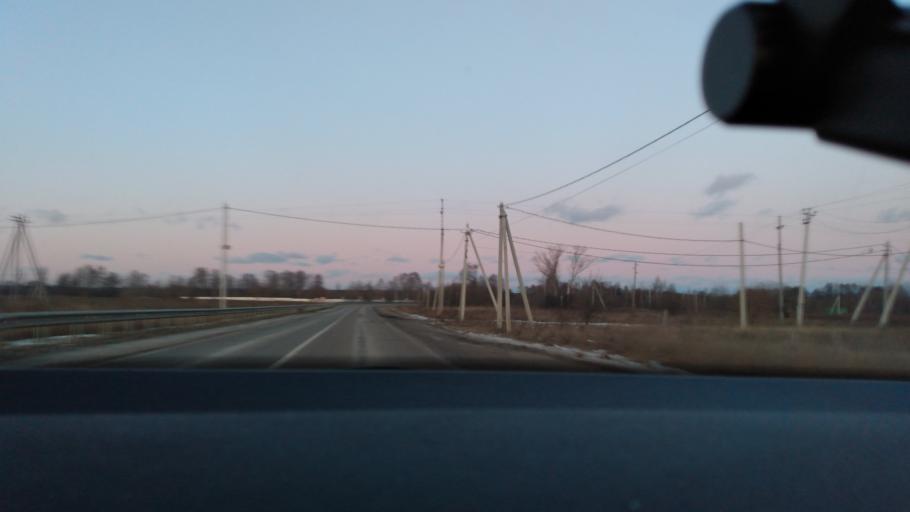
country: RU
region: Moskovskaya
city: Krasnaya Poyma
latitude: 55.1238
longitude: 39.0771
